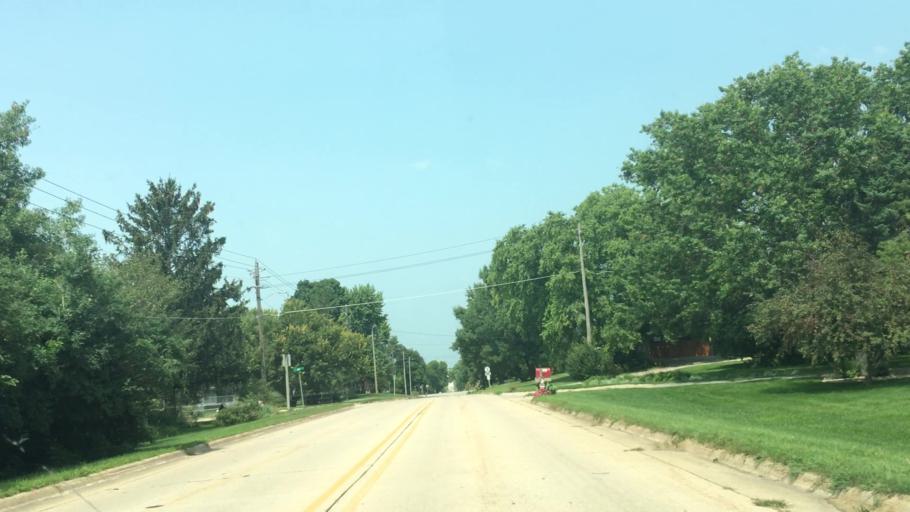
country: US
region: Iowa
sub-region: Fayette County
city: Oelwein
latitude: 42.6769
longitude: -91.8936
